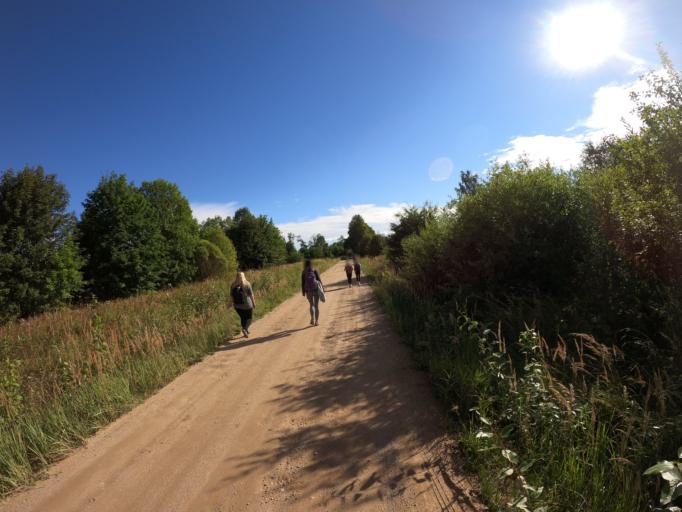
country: LV
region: Talsu Rajons
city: Stende
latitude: 57.0664
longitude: 22.2993
